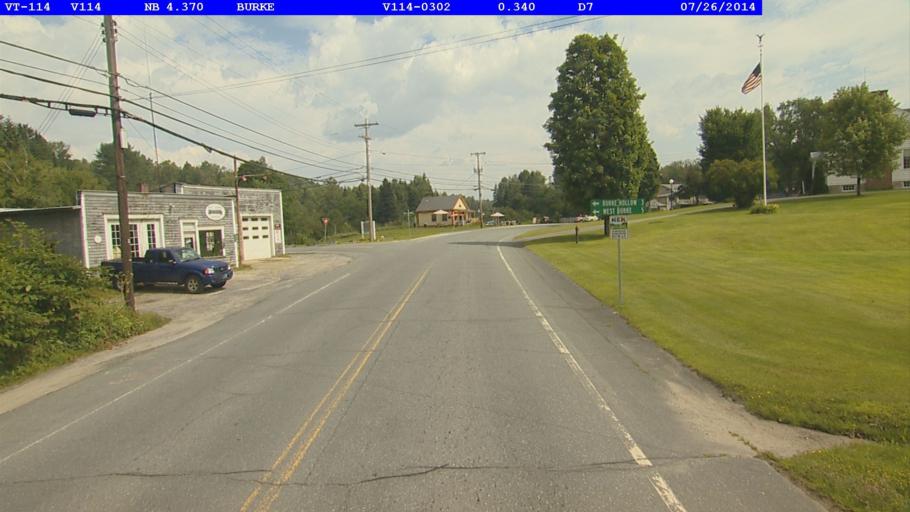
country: US
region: Vermont
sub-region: Caledonia County
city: Lyndonville
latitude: 44.5872
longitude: -71.9468
